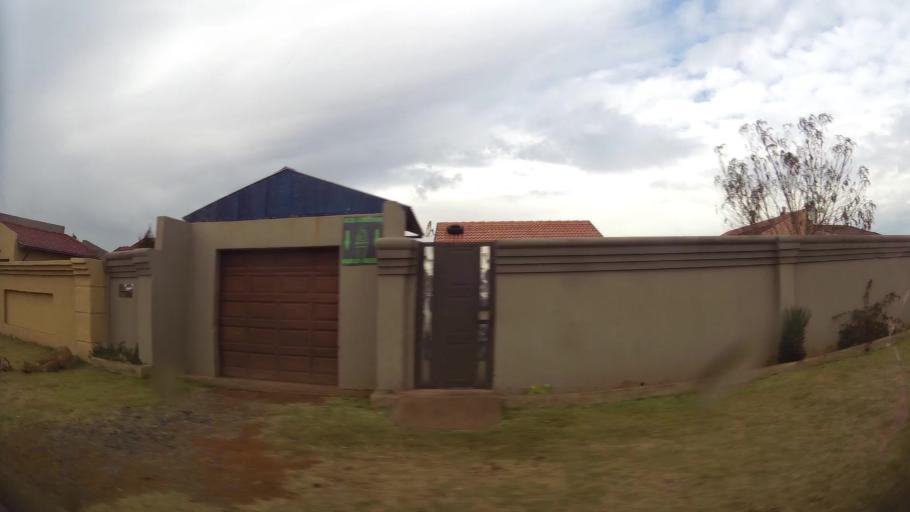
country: ZA
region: Gauteng
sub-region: Ekurhuleni Metropolitan Municipality
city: Germiston
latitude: -26.3255
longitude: 28.1959
